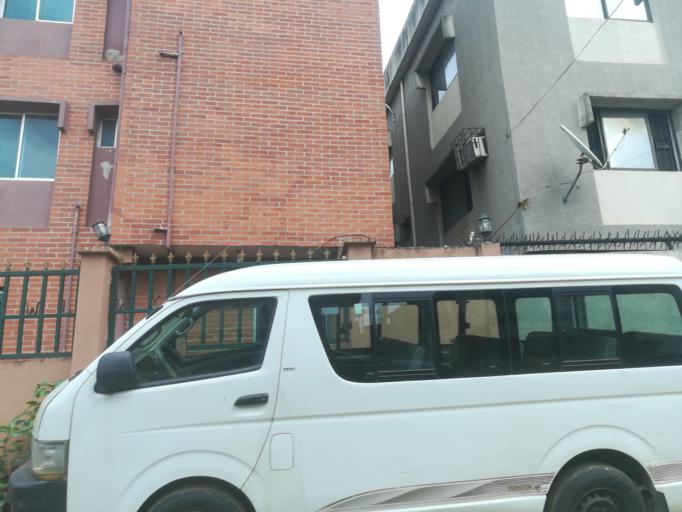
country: NG
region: Lagos
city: Somolu
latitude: 6.5478
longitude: 3.3896
